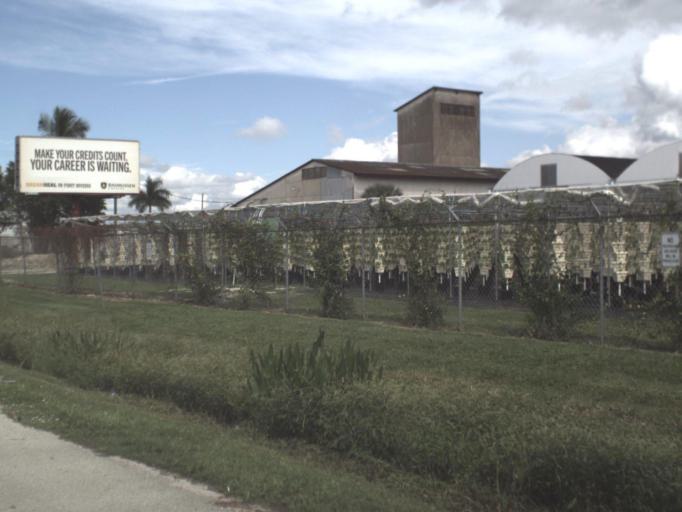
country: US
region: Florida
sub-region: Lee County
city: Fort Myers
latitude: 26.6176
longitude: -81.8519
